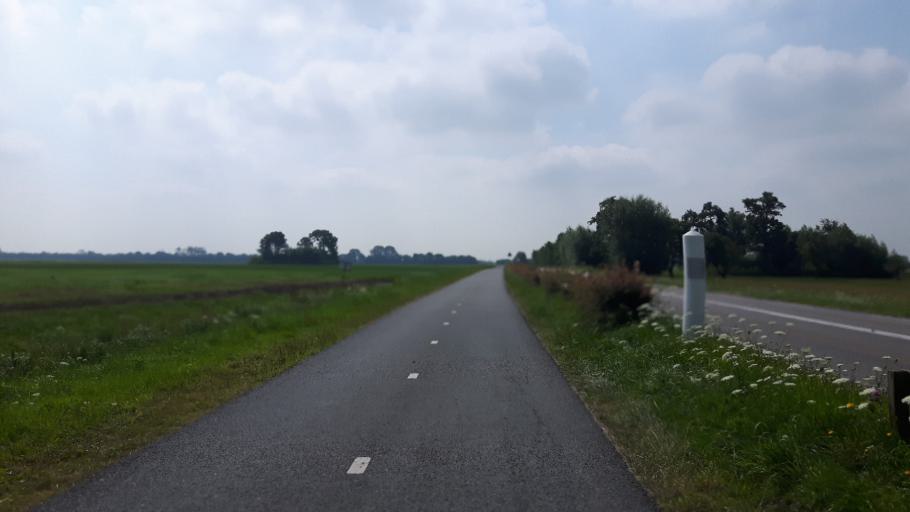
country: NL
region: Utrecht
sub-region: Gemeente Montfoort
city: Montfoort
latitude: 52.0253
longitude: 4.9469
